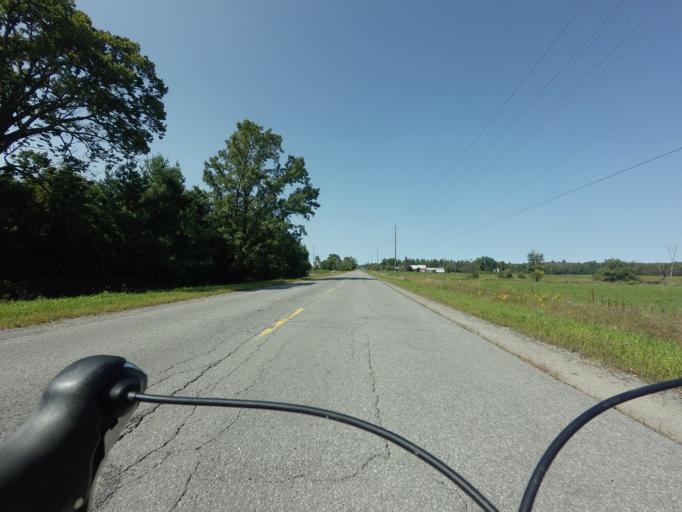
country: CA
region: Ontario
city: Arnprior
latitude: 45.4866
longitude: -76.1310
